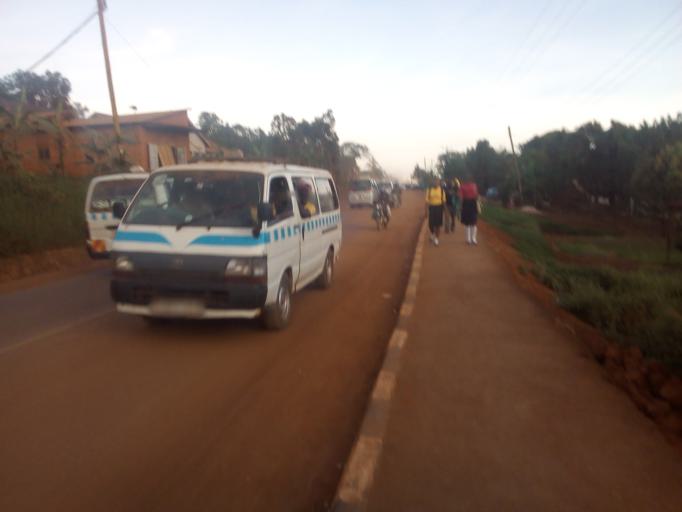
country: UG
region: Central Region
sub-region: Wakiso District
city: Kajansi
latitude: 0.2398
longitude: 32.5738
